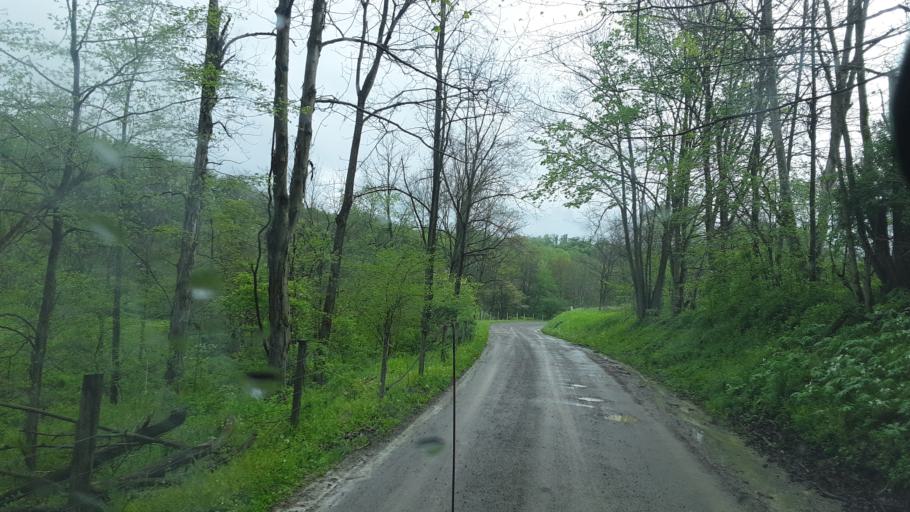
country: US
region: Ohio
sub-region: Holmes County
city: Millersburg
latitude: 40.4961
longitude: -81.8348
